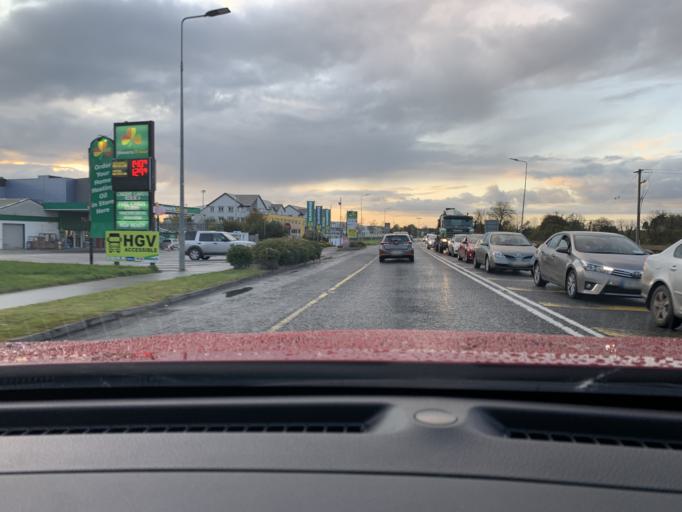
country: IE
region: Connaught
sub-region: County Leitrim
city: Carrick-on-Shannon
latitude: 53.9420
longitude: -8.1053
